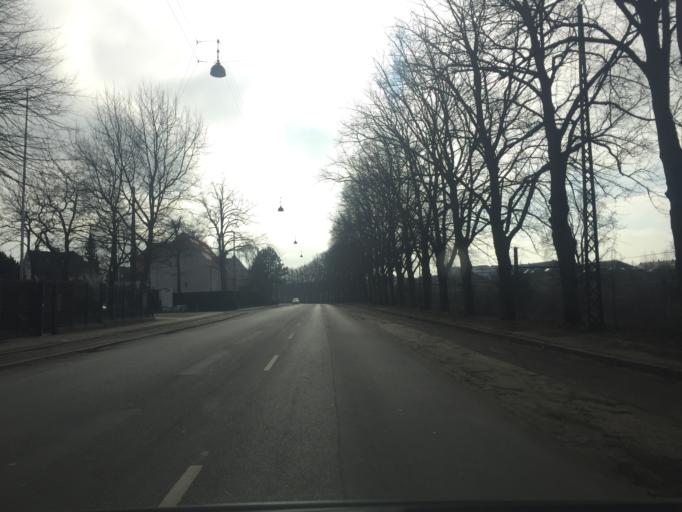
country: DK
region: Capital Region
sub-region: Gentofte Kommune
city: Charlottenlund
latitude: 55.7207
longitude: 12.5719
